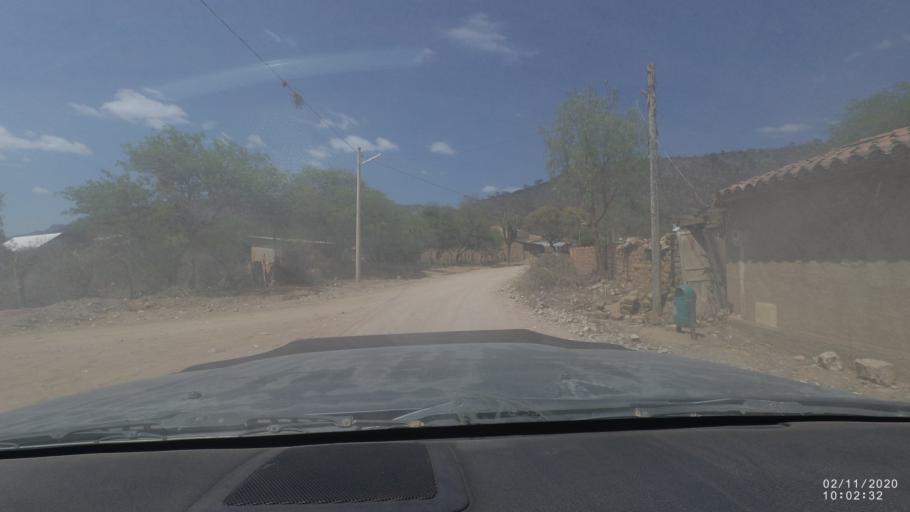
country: BO
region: Chuquisaca
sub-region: Provincia Zudanez
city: Mojocoya
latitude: -18.3247
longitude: -64.6724
